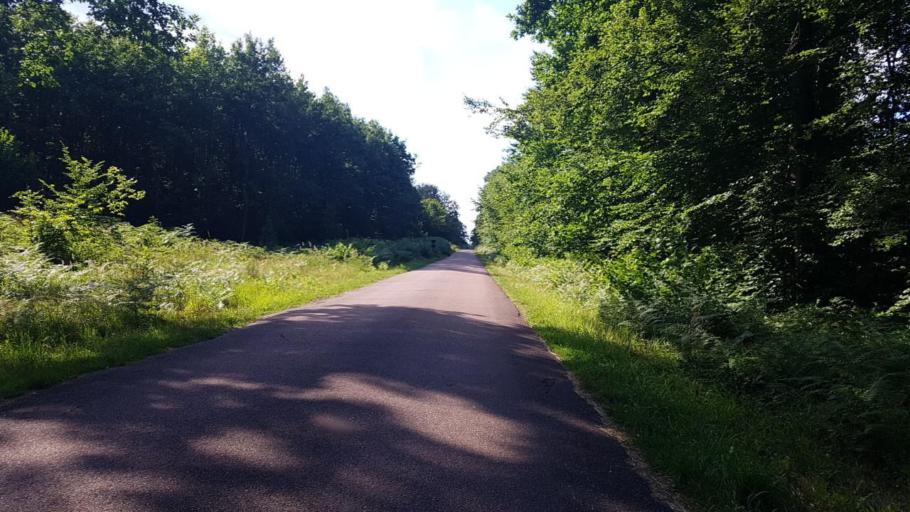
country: FR
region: Picardie
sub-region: Departement de l'Oise
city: Ver-sur-Launette
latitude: 49.1427
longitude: 2.6521
